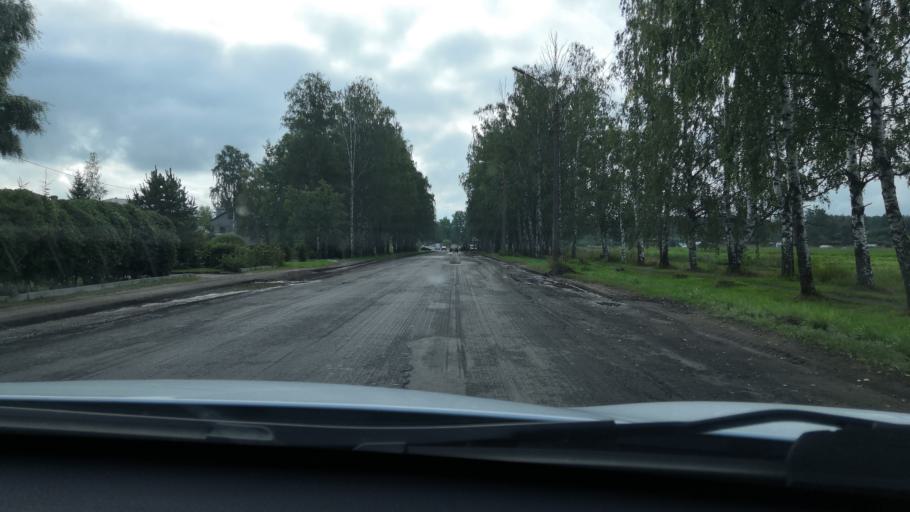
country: RU
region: St.-Petersburg
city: Tyarlevo
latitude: 59.7129
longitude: 30.4626
